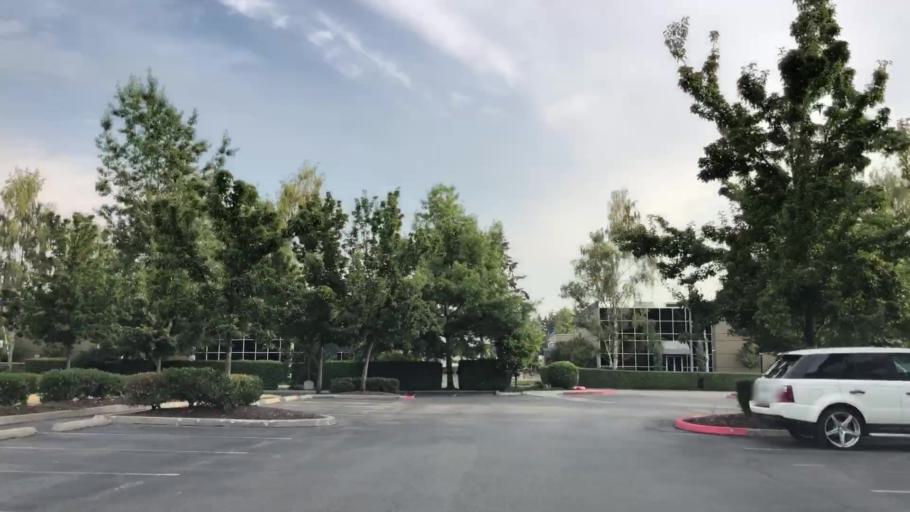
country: US
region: Washington
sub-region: King County
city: Bothell
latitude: 47.7944
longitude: -122.2029
